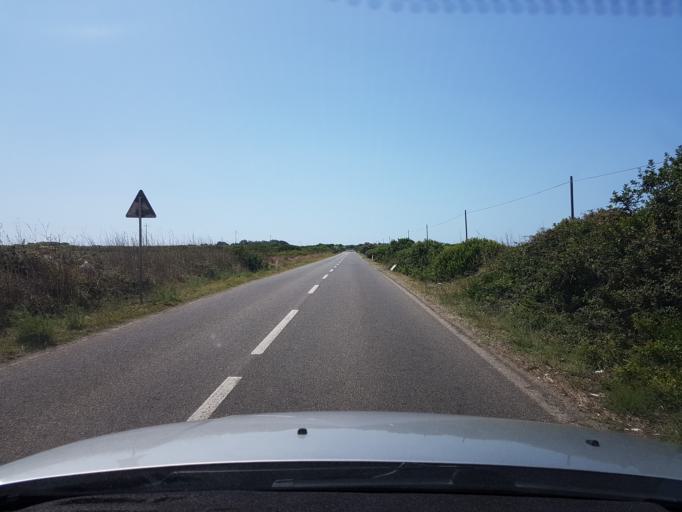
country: IT
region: Sardinia
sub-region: Provincia di Oristano
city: Riola Sardo
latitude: 40.0223
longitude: 8.4697
